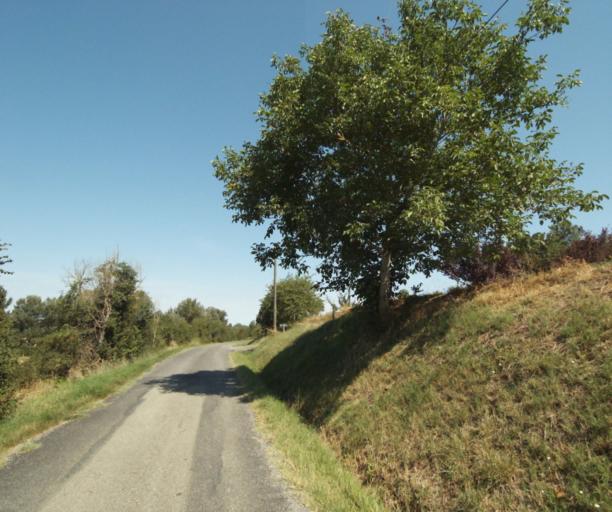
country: FR
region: Midi-Pyrenees
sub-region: Departement de l'Ariege
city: Lezat-sur-Leze
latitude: 43.2641
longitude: 1.3624
